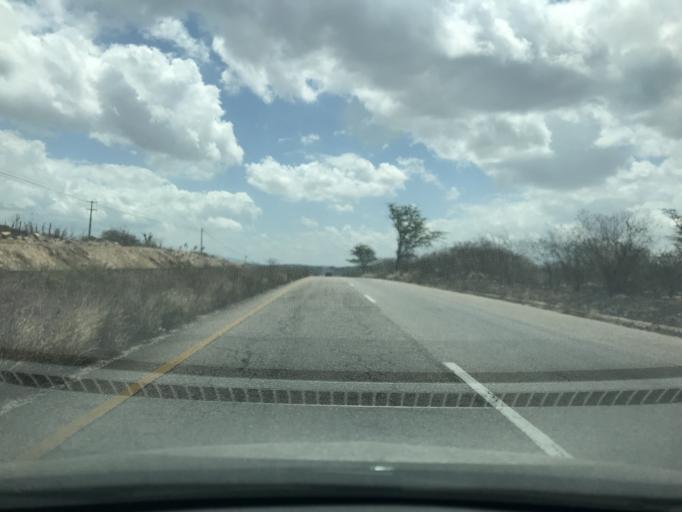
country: BR
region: Pernambuco
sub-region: Caruaru
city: Caruaru
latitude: -8.2983
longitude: -35.9023
